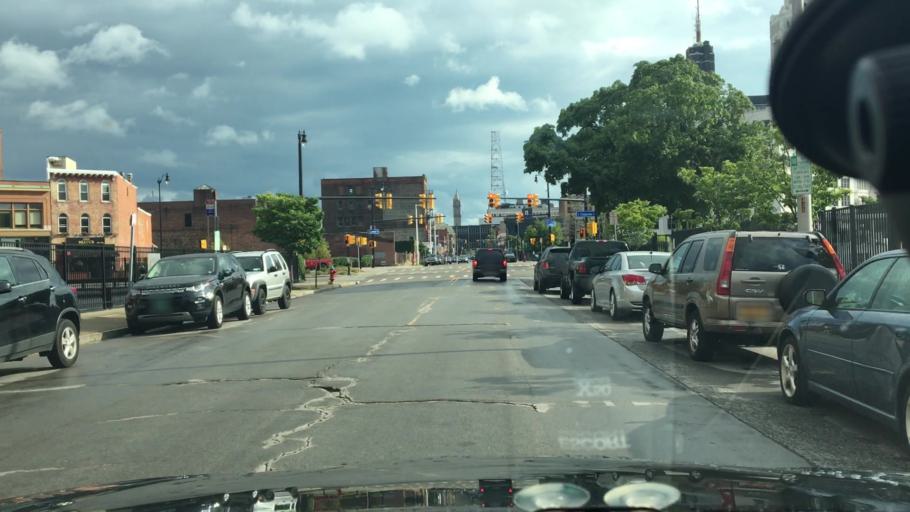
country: US
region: New York
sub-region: Erie County
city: Buffalo
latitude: 42.8902
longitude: -78.8706
